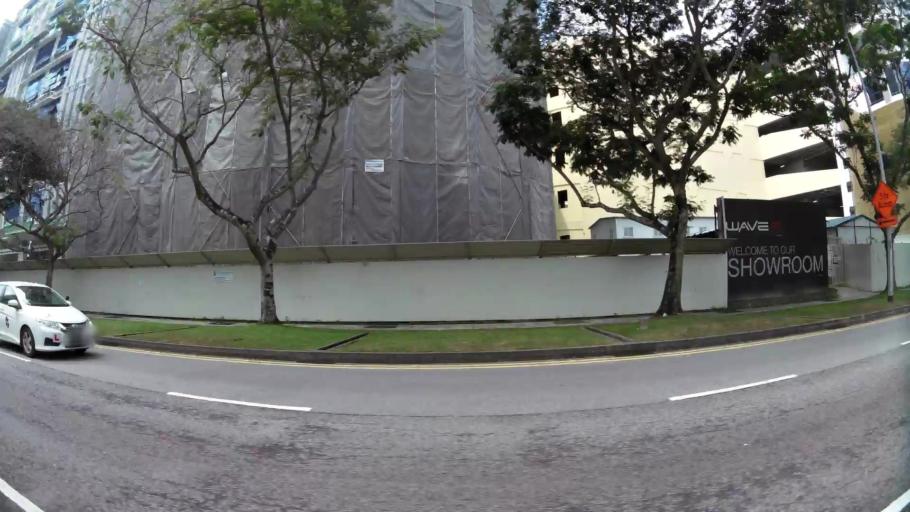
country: MY
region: Johor
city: Johor Bahru
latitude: 1.4482
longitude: 103.7983
